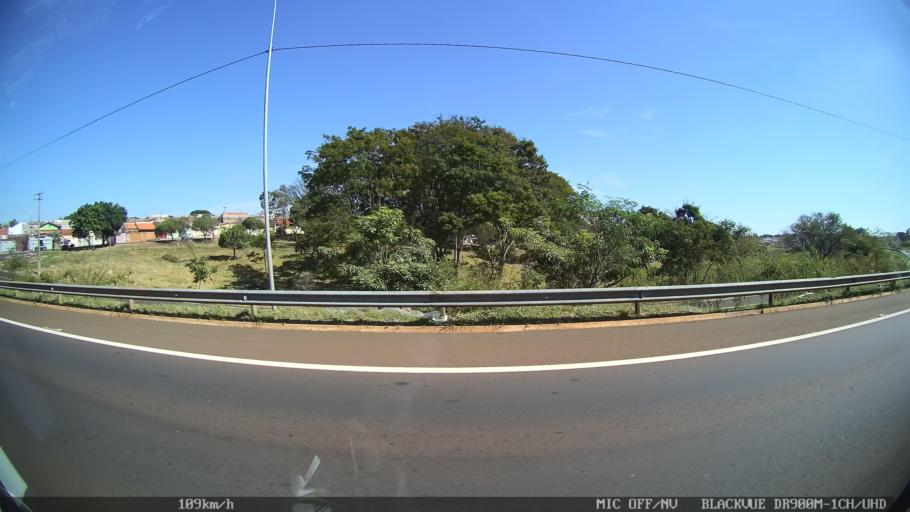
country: BR
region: Sao Paulo
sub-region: Franca
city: Franca
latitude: -20.4858
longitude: -47.4093
